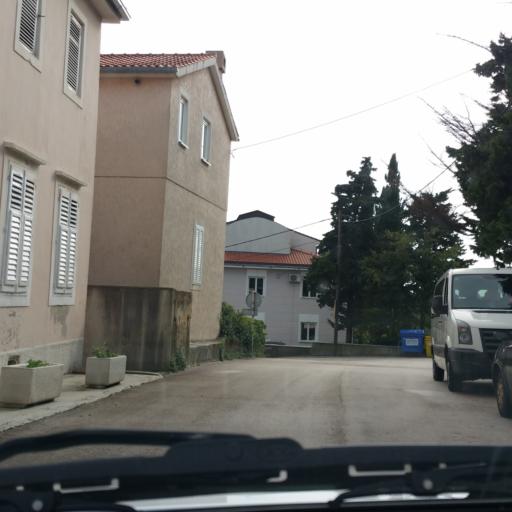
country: HR
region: Primorsko-Goranska
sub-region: Grad Krk
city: Krk
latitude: 45.0268
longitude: 14.5719
